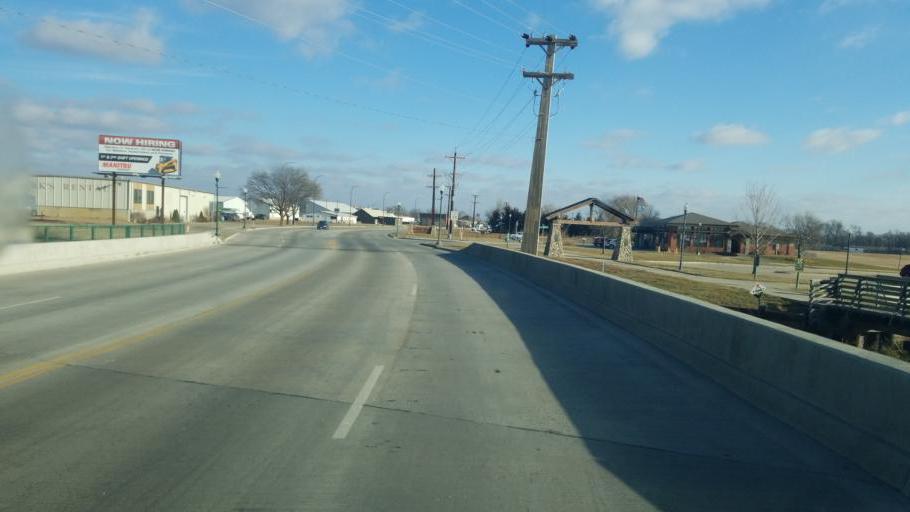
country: US
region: South Dakota
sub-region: Yankton County
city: Yankton
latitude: 42.8715
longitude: -97.3815
